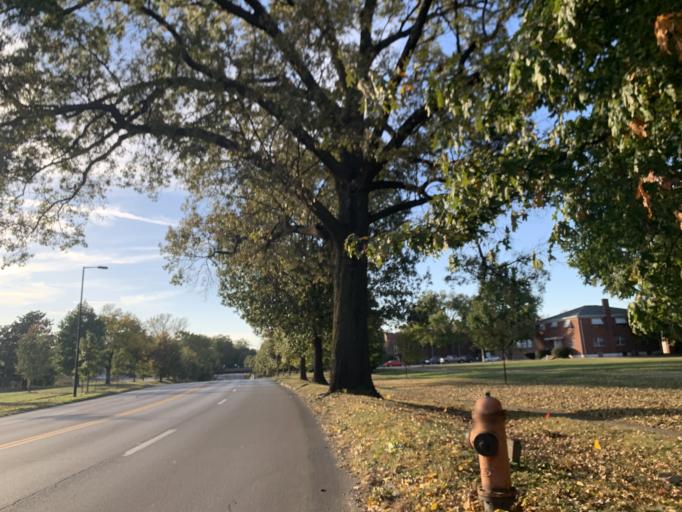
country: US
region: Kentucky
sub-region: Jefferson County
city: Louisville
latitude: 38.2211
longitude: -85.7787
